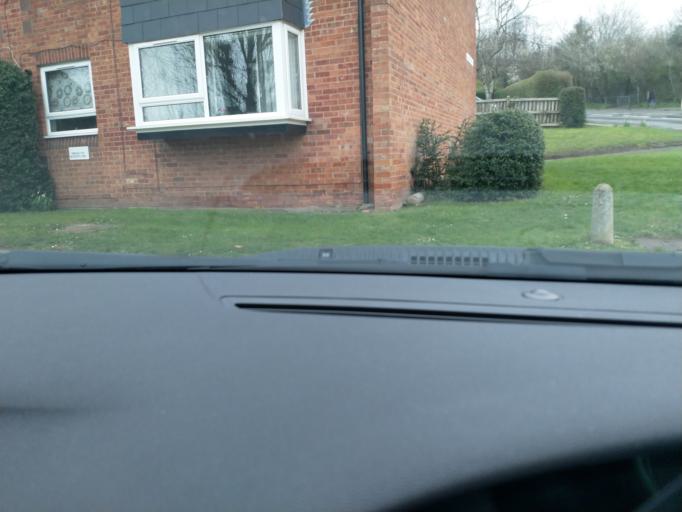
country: GB
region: England
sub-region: Warwickshire
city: Royal Leamington Spa
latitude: 52.2945
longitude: -1.5241
